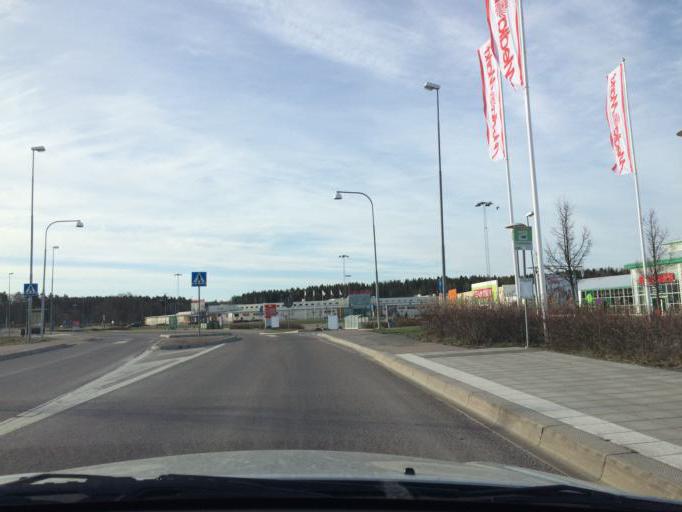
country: SE
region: Soedermanland
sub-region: Eskilstuna Kommun
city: Eskilstuna
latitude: 59.3743
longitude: 16.4694
